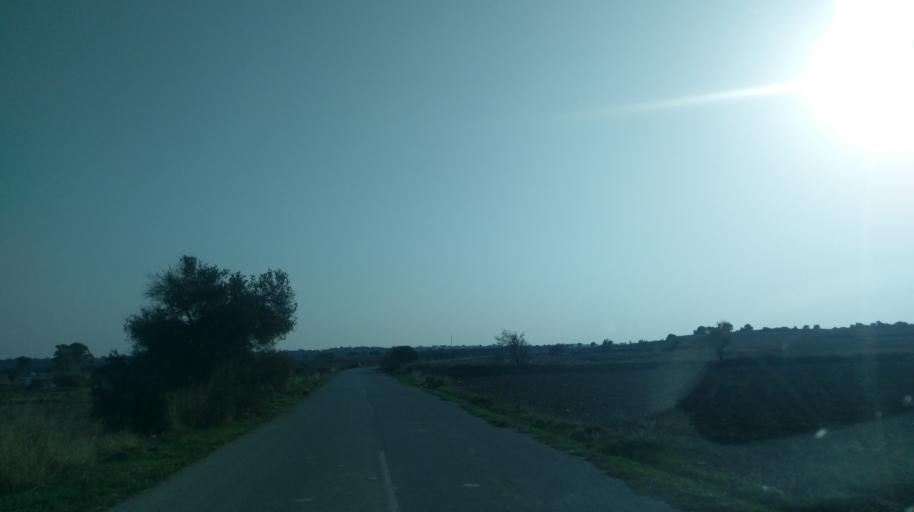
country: CY
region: Ammochostos
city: Leonarisso
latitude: 35.4421
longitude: 34.0882
